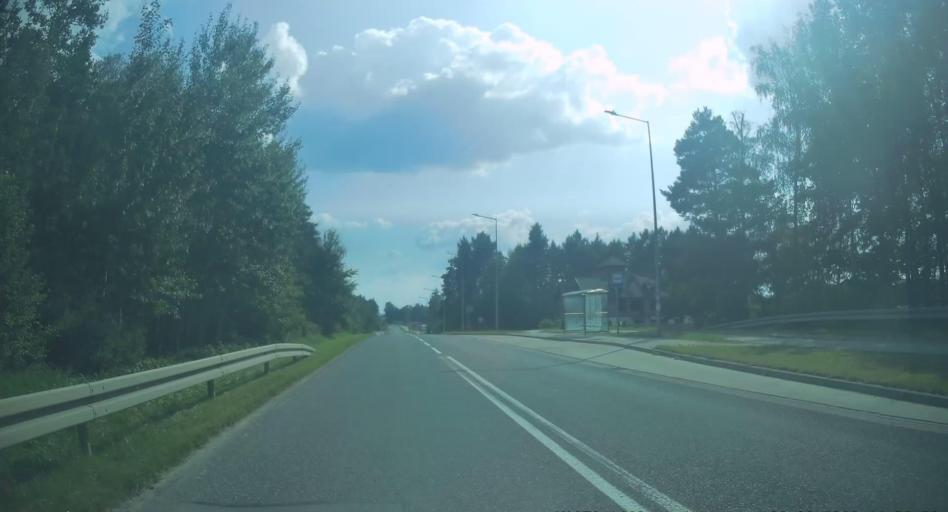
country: PL
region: Swietokrzyskie
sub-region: Powiat kielecki
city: Lopuszno
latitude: 50.9410
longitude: 20.2451
